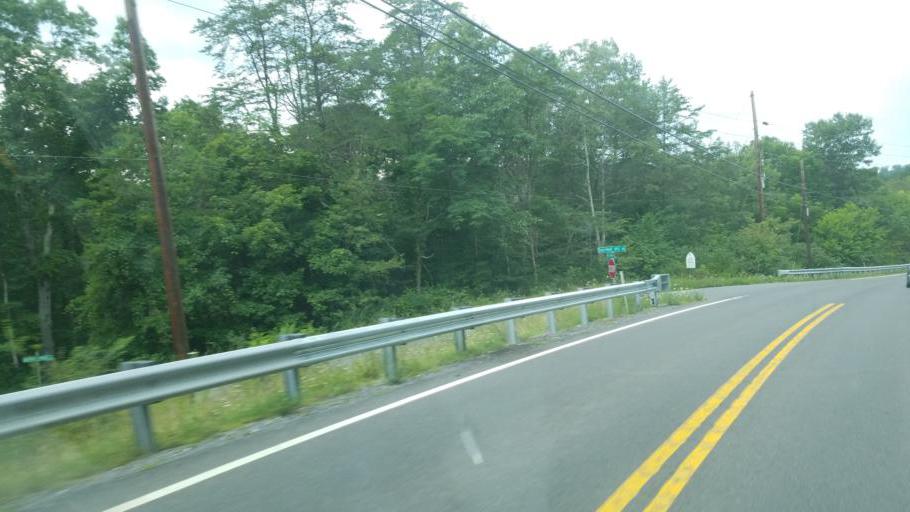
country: US
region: West Virginia
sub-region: Morgan County
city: Berkeley Springs
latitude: 39.5370
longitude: -78.4752
